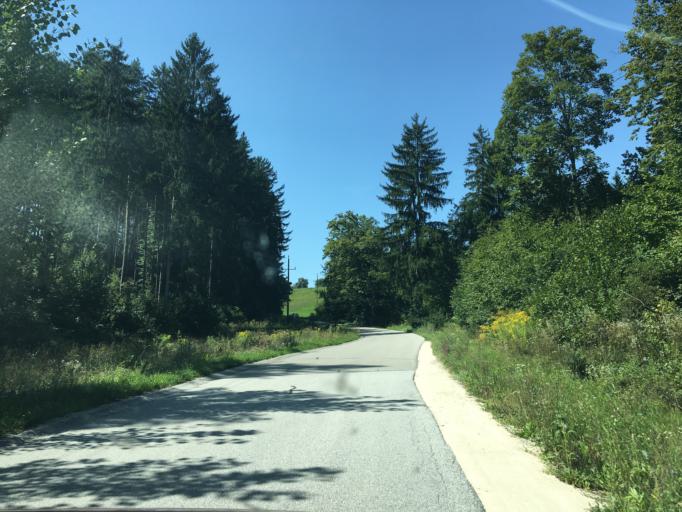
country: AT
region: Carinthia
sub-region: Politischer Bezirk Volkermarkt
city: Eberndorf
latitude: 46.5915
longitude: 14.6256
